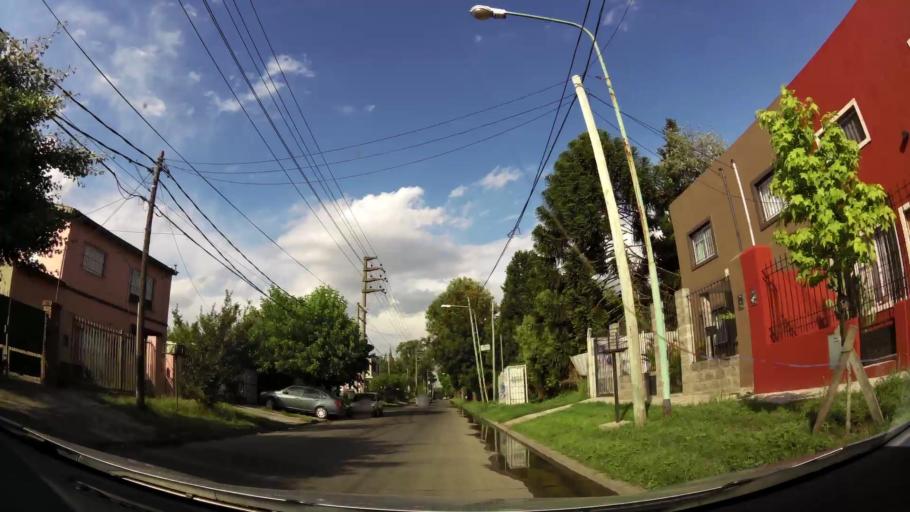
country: AR
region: Buenos Aires
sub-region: Partido de Tigre
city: Tigre
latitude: -34.4728
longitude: -58.6520
